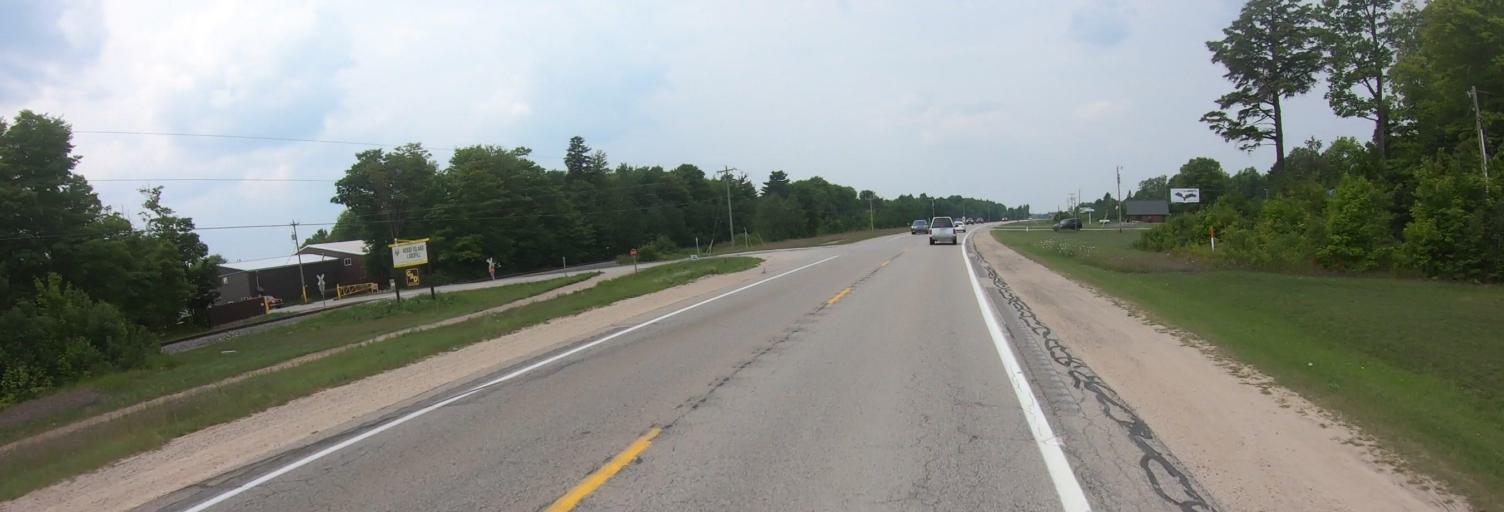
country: US
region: Michigan
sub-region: Alger County
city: Munising
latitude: 46.3772
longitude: -86.5941
